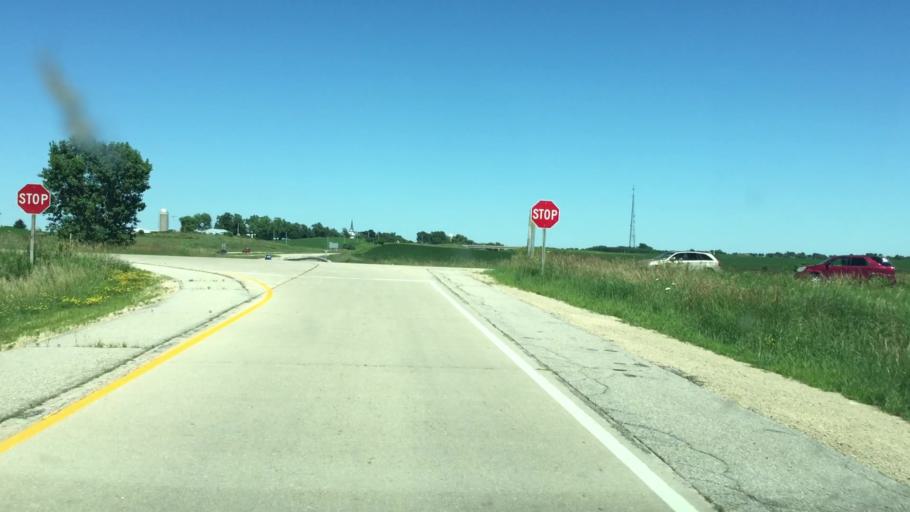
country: US
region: Wisconsin
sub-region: Dane County
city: Mount Horeb
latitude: 43.0037
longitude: -89.7027
